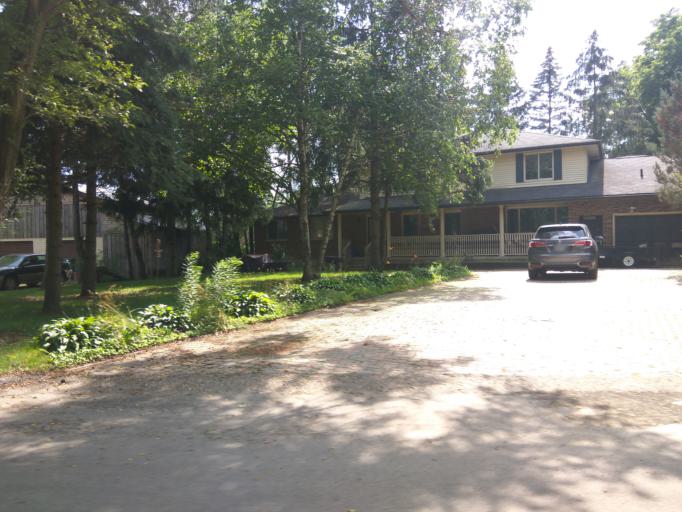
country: CA
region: Ontario
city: Cambridge
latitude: 43.4009
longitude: -80.3836
